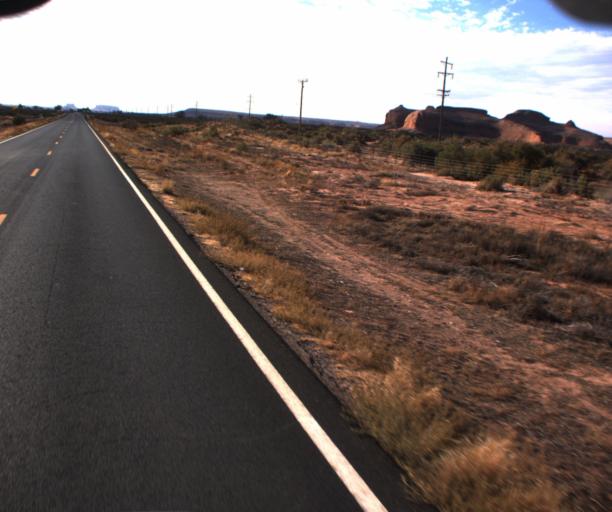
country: US
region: Arizona
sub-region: Apache County
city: Many Farms
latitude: 36.7316
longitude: -109.6323
